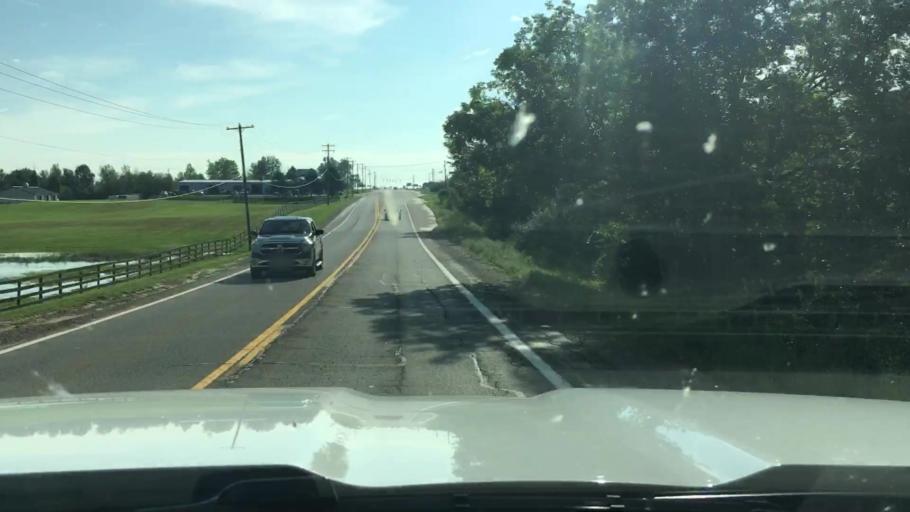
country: US
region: Michigan
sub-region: Kent County
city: Cedar Springs
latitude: 43.2198
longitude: -85.5856
